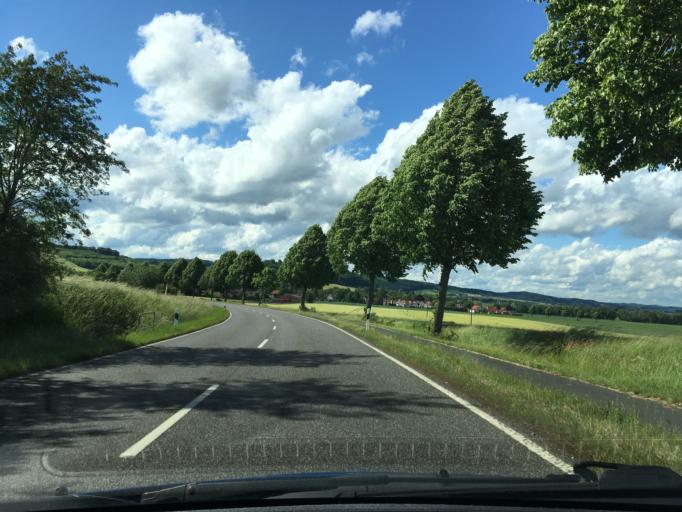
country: DE
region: Lower Saxony
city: Bovenden
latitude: 51.5933
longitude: 9.8677
